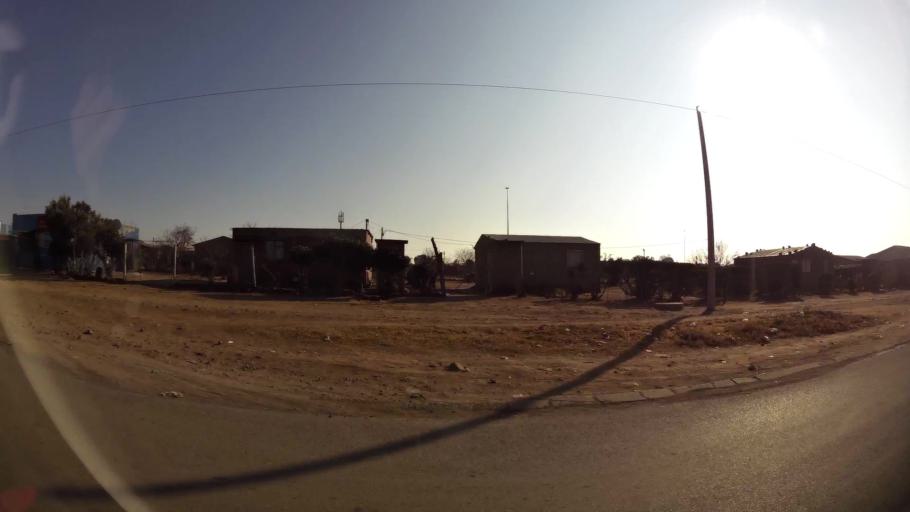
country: ZA
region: Orange Free State
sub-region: Mangaung Metropolitan Municipality
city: Bloemfontein
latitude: -29.1952
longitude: 26.2685
